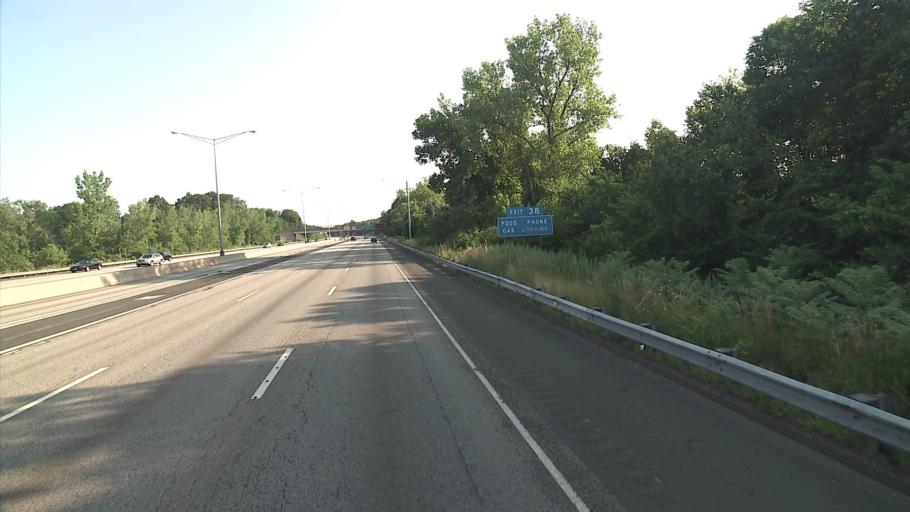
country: US
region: Connecticut
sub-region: Hartford County
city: Windsor
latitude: 41.8599
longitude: -72.6627
